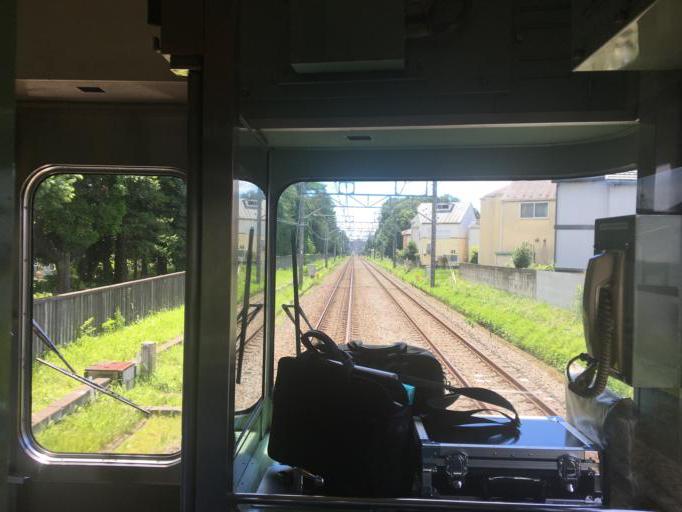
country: JP
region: Tokyo
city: Higashimurayama-shi
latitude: 35.7451
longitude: 139.4780
